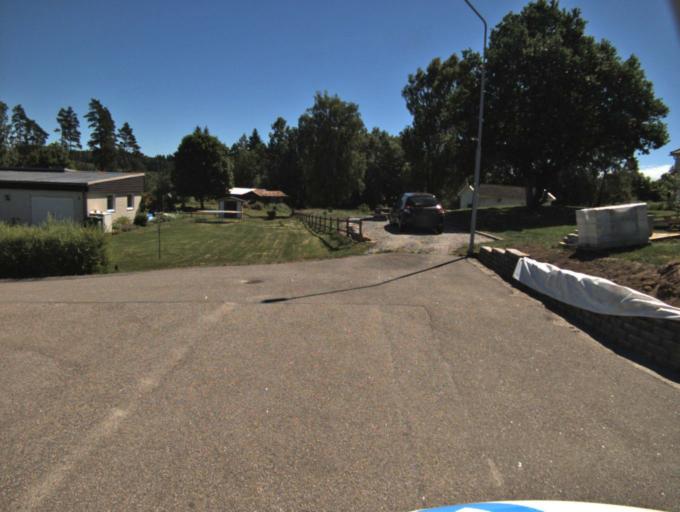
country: SE
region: Vaestra Goetaland
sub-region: Ulricehamns Kommun
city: Ulricehamn
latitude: 57.6662
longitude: 13.4344
